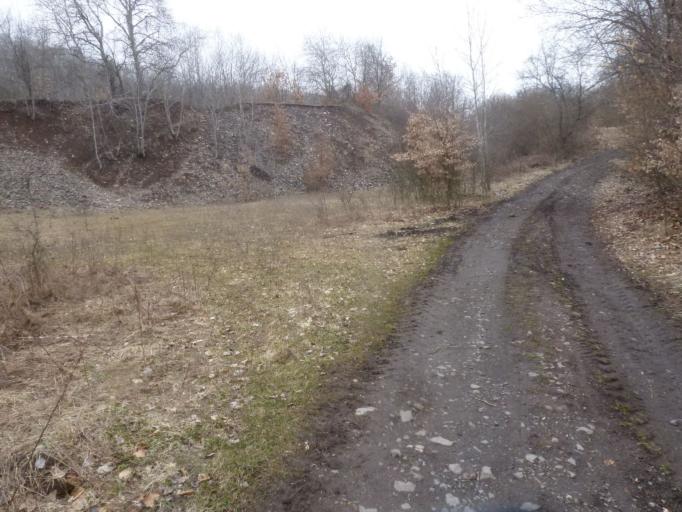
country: HU
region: Nograd
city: Somoskoujfalu
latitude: 48.1691
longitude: 19.8643
